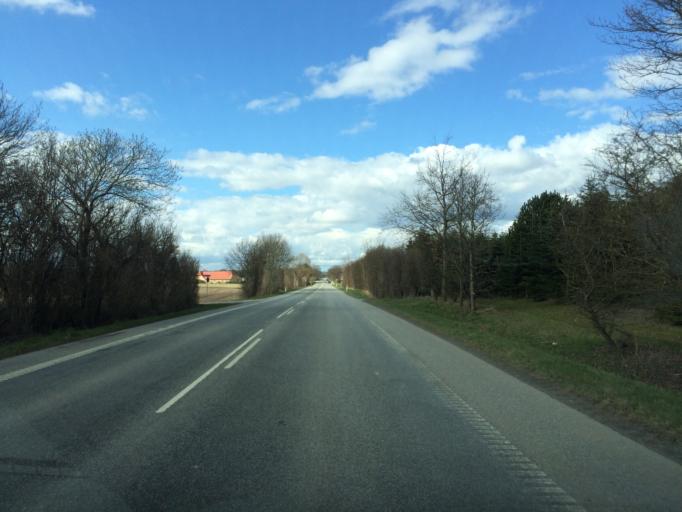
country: DK
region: South Denmark
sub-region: Middelfart Kommune
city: Brenderup
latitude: 55.4368
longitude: 10.0016
